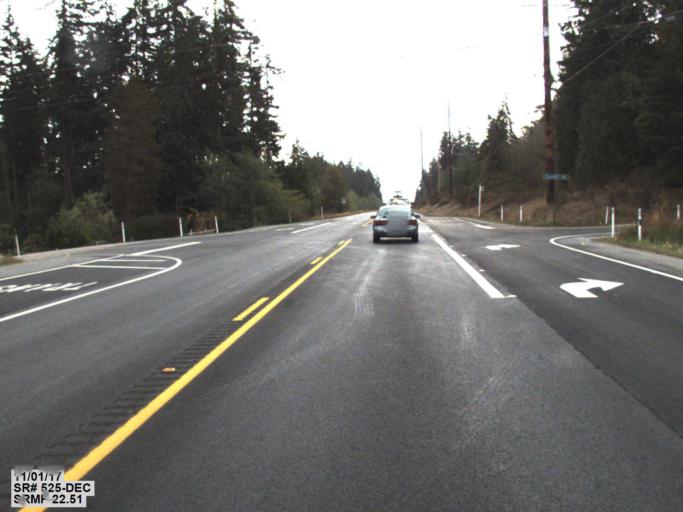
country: US
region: Washington
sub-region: Island County
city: Freeland
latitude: 48.0620
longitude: -122.5668
